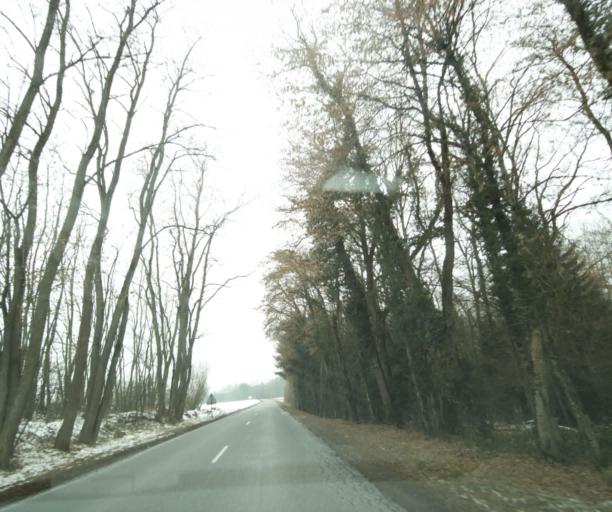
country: FR
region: Rhone-Alpes
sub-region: Departement de la Haute-Savoie
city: Contamine-sur-Arve
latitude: 46.1263
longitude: 6.3069
